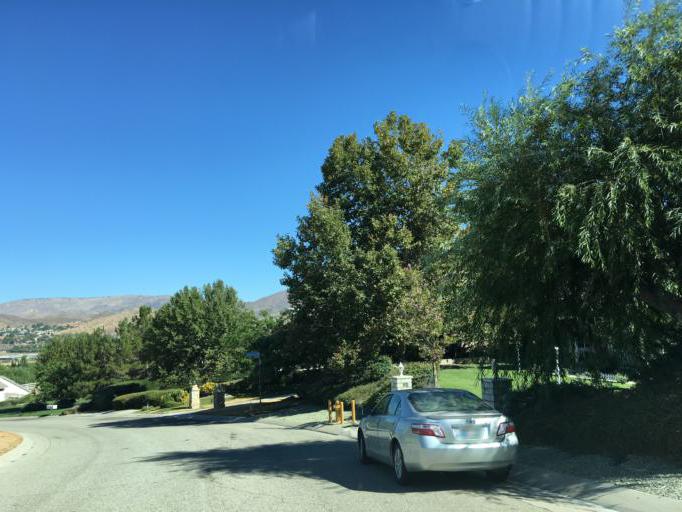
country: US
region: California
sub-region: Los Angeles County
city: Acton
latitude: 34.4705
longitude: -118.1548
